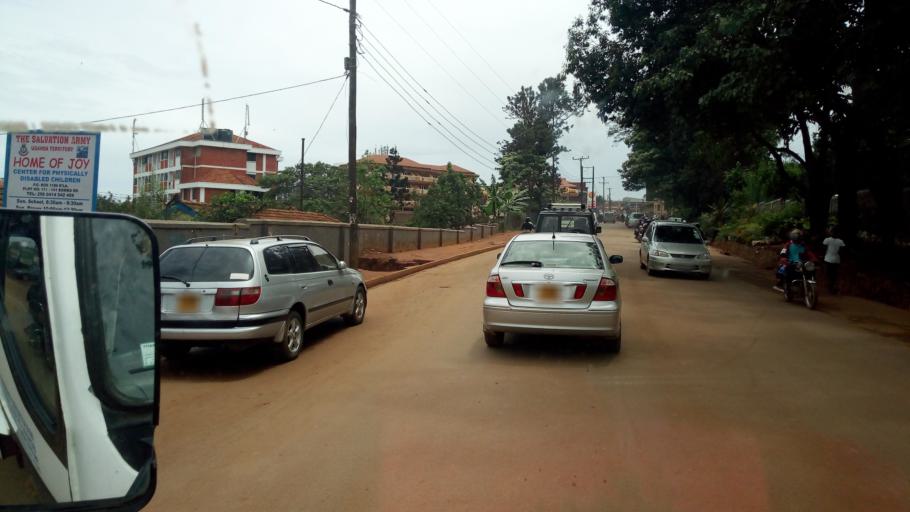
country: UG
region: Central Region
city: Kampala Central Division
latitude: 0.3372
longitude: 32.5723
